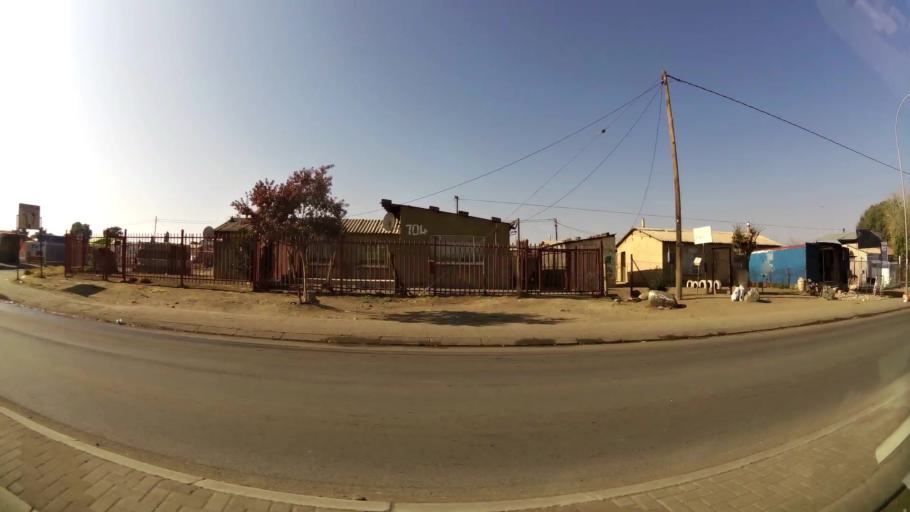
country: ZA
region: Orange Free State
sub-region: Mangaung Metropolitan Municipality
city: Bloemfontein
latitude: -29.1635
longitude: 26.2377
